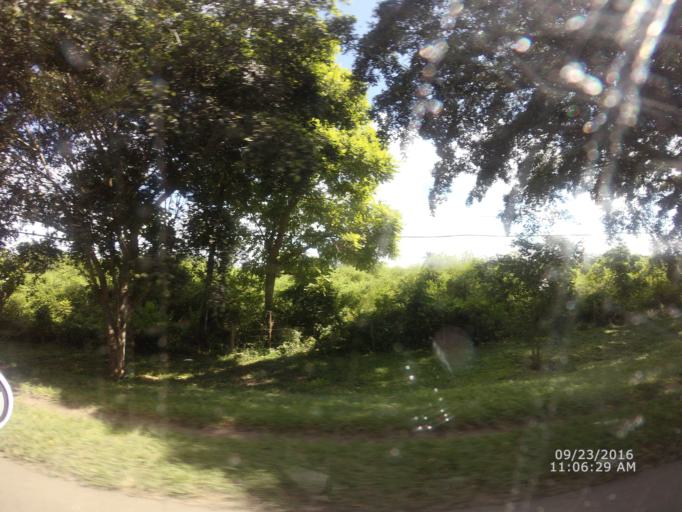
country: CU
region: Mayabeque
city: Jamaica
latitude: 23.0112
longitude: -82.2225
